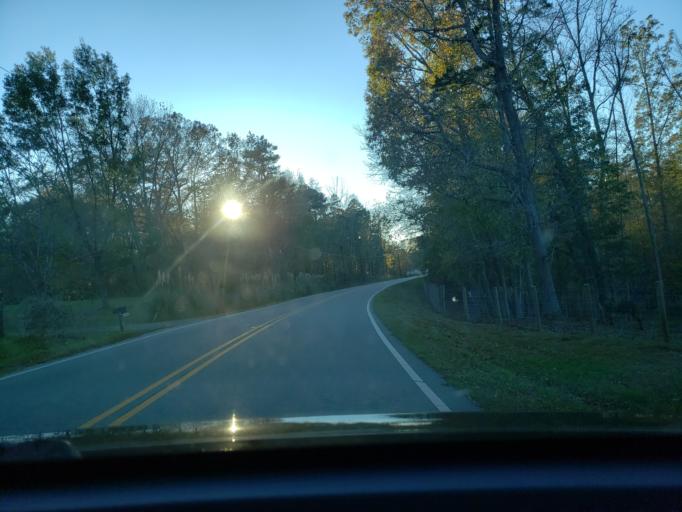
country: US
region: North Carolina
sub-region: Forsyth County
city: Walkertown
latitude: 36.2221
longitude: -80.1738
